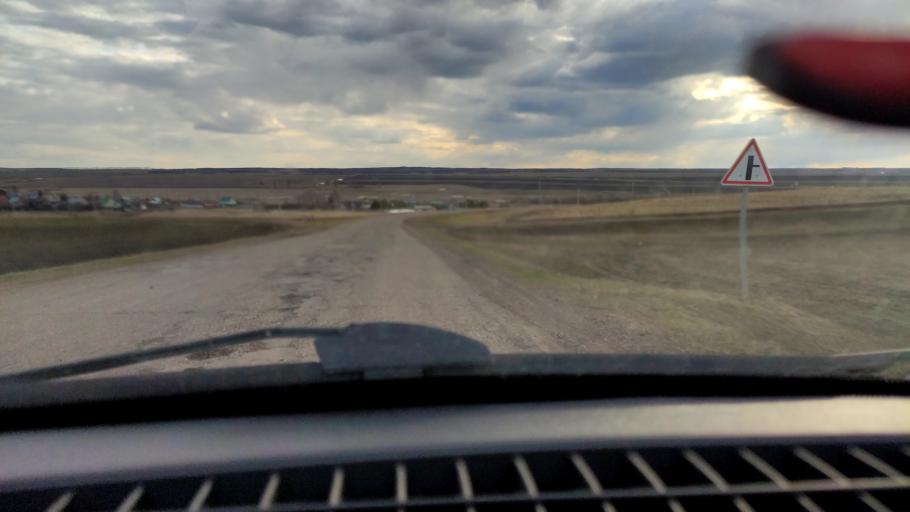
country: RU
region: Bashkortostan
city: Tolbazy
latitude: 54.2933
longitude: 55.9109
